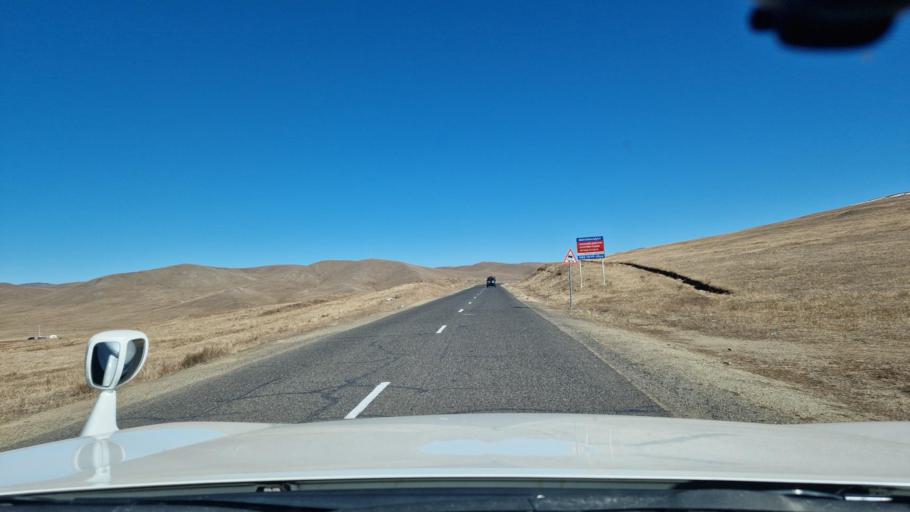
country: MN
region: Hentiy
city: Modot
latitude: 47.8090
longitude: 108.7883
